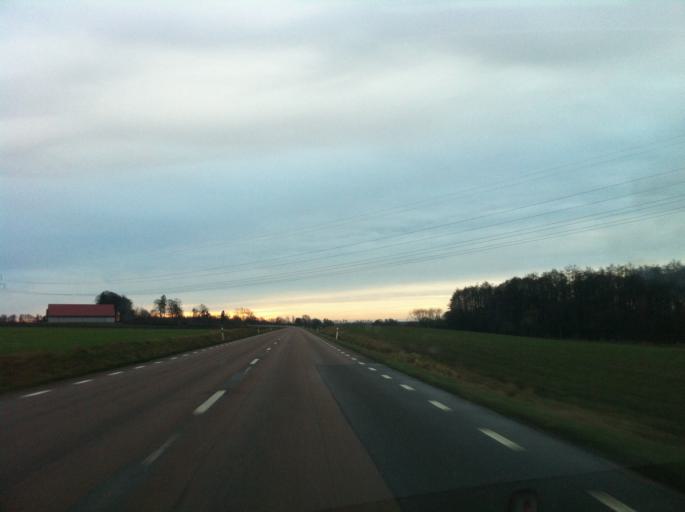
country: SE
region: Skane
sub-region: Bjuvs Kommun
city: Billesholm
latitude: 55.9882
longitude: 12.9400
